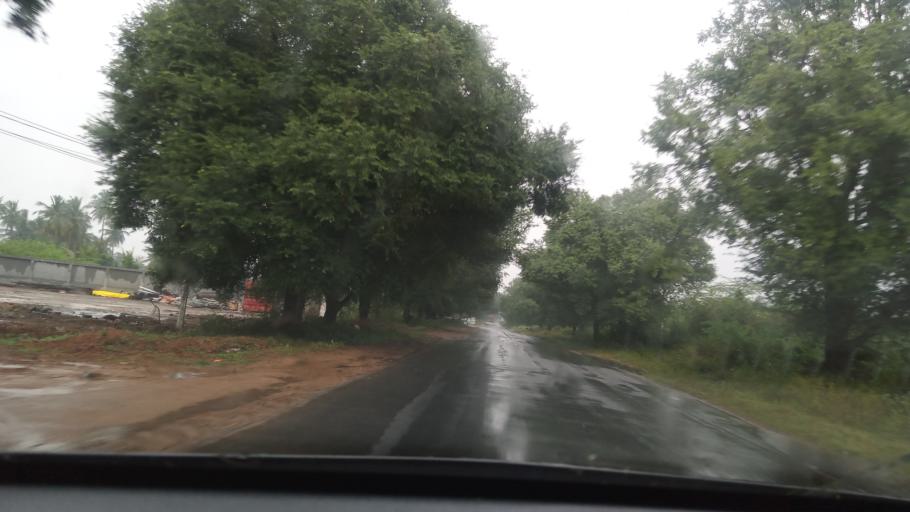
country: IN
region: Tamil Nadu
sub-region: Vellore
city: Walajapet
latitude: 12.8515
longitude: 79.3877
